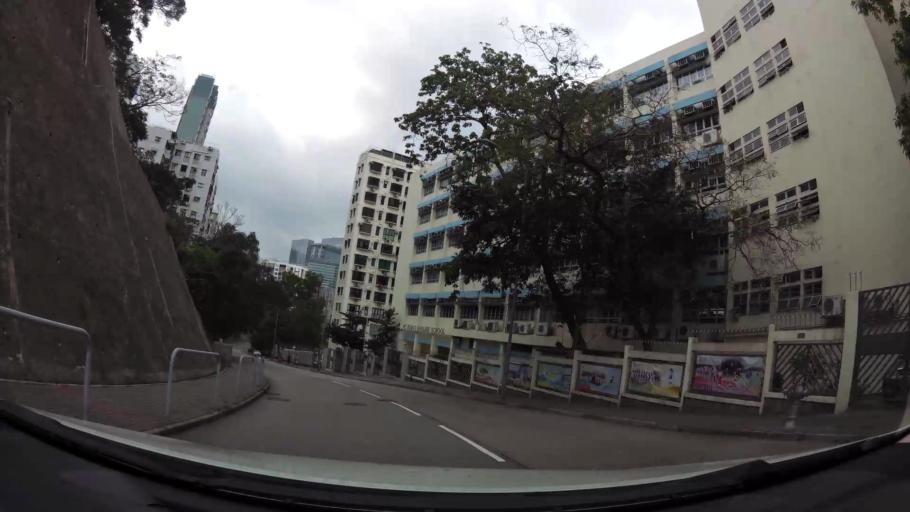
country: HK
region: Kowloon City
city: Kowloon
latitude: 22.3187
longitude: 114.2188
